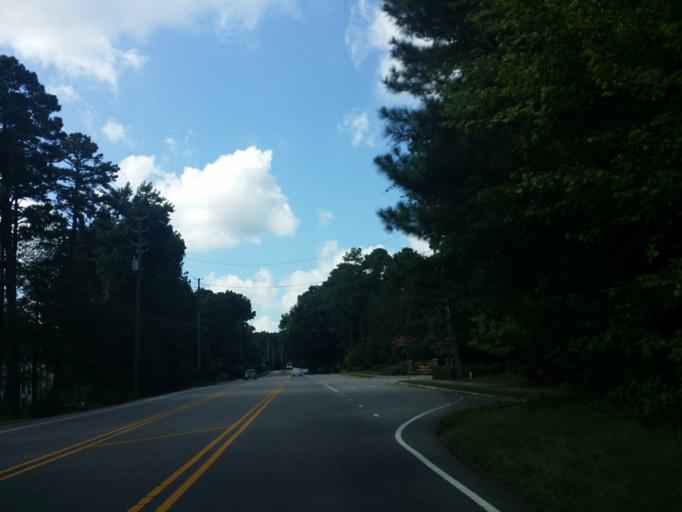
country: US
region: North Carolina
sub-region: Wake County
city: West Raleigh
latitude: 35.8821
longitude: -78.7087
